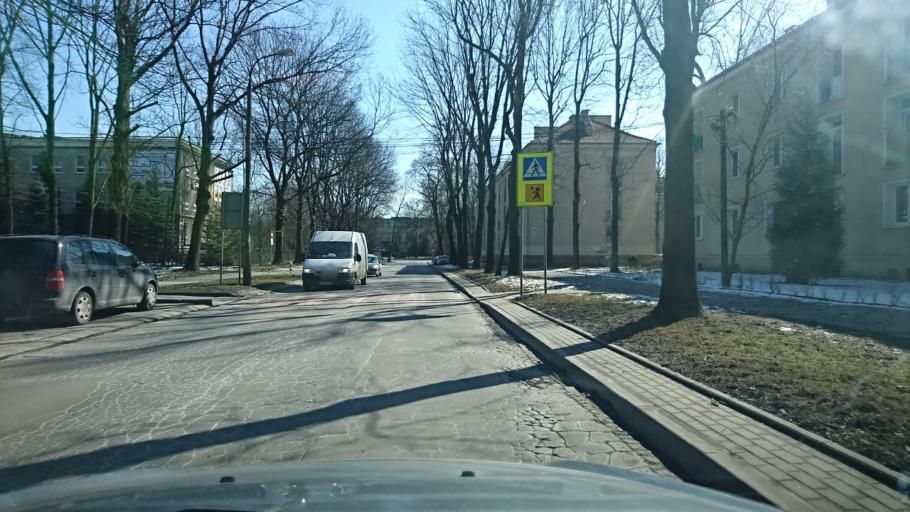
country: PL
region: Lesser Poland Voivodeship
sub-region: Powiat wielicki
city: Kokotow
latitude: 50.0728
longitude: 20.0519
